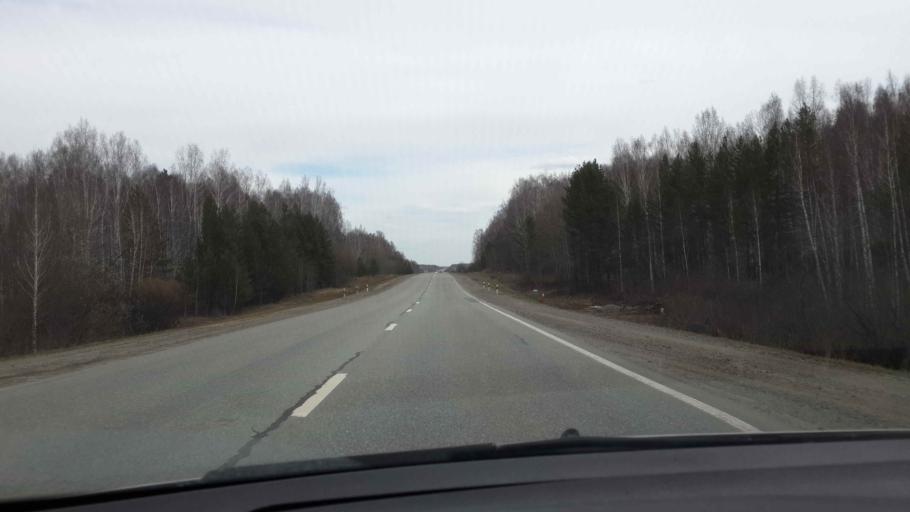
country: RU
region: Sverdlovsk
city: Baraba
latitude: 56.7786
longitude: 61.8042
